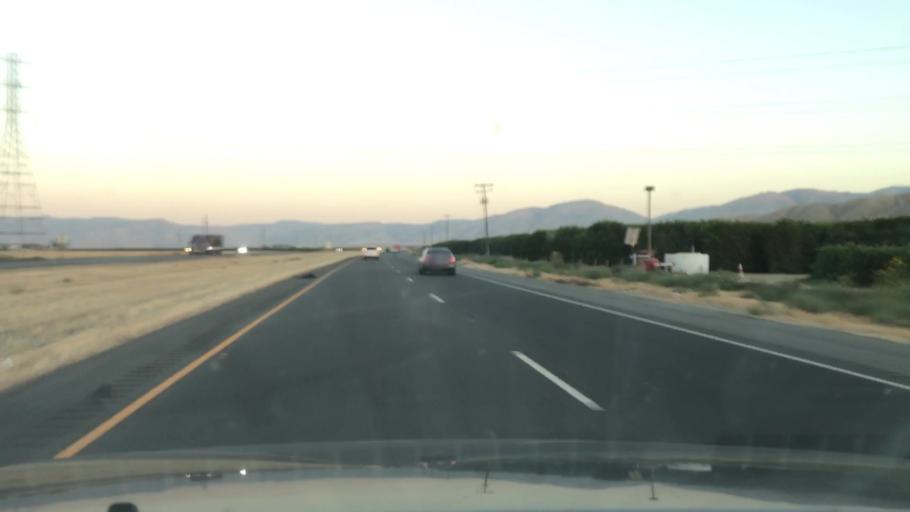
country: US
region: California
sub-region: Kern County
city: Weedpatch
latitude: 35.0494
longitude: -118.9888
